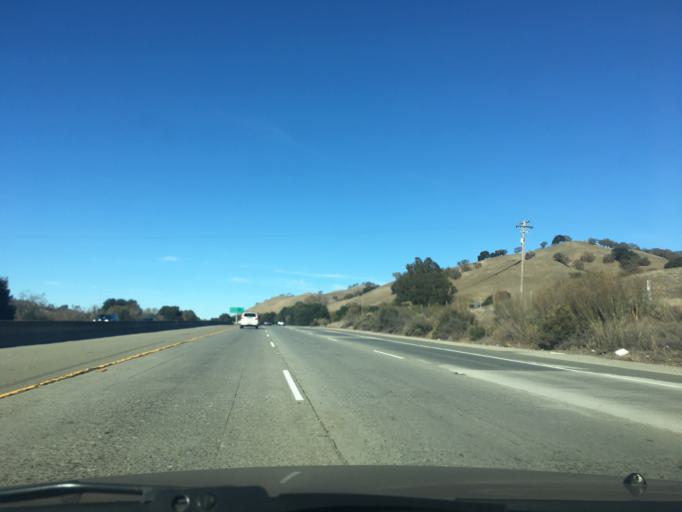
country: US
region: California
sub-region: Alameda County
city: Pleasanton
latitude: 37.6093
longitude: -121.8739
